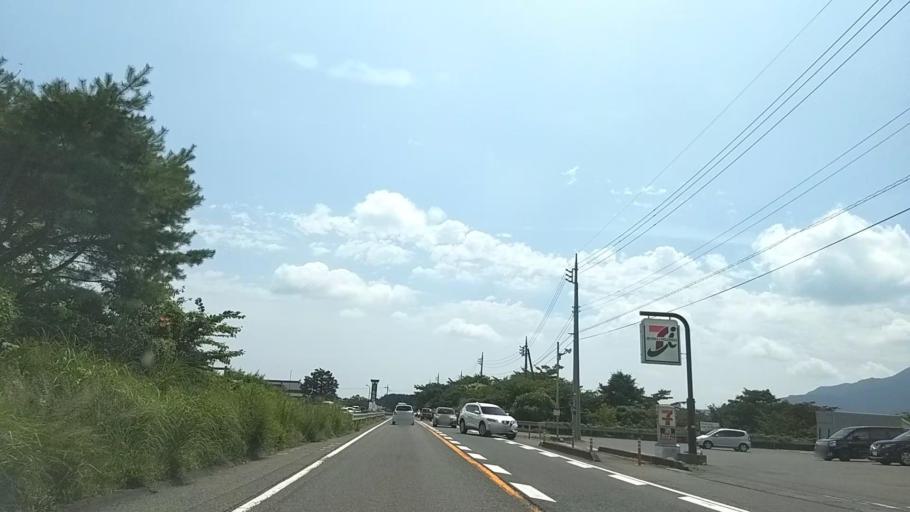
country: JP
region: Yamanashi
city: Fujikawaguchiko
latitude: 35.3732
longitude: 138.5760
